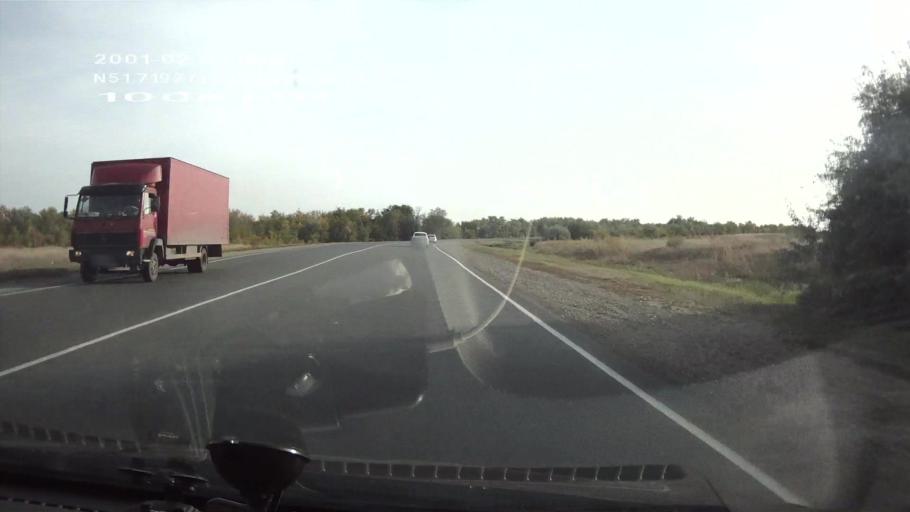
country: RU
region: Saratov
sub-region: Saratovskiy Rayon
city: Saratov
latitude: 51.7200
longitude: 46.0262
